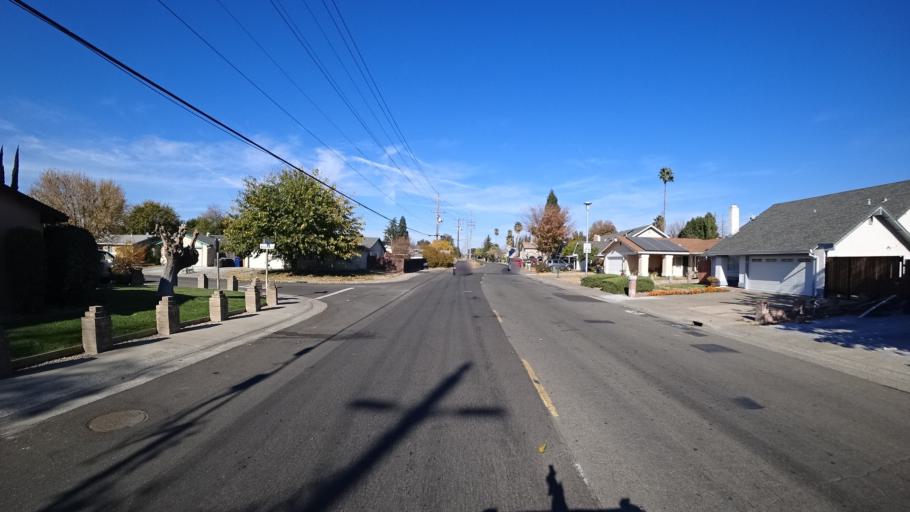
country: US
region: California
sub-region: Sacramento County
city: Antelope
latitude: 38.6991
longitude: -121.3265
